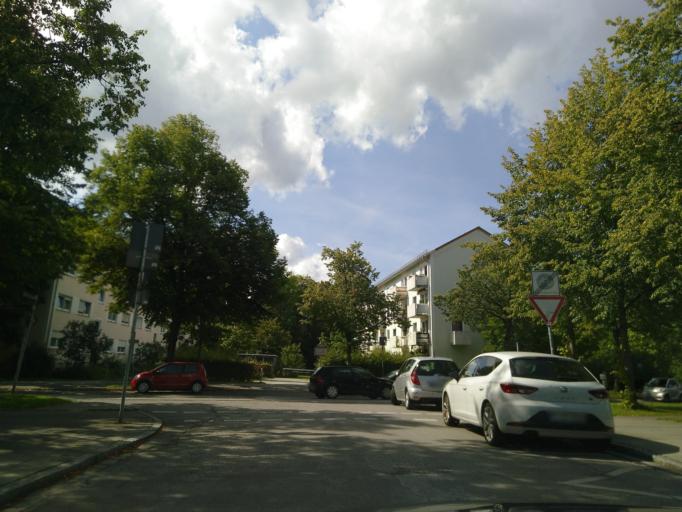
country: DE
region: Bavaria
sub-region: Upper Bavaria
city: Munich
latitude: 48.1212
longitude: 11.5318
